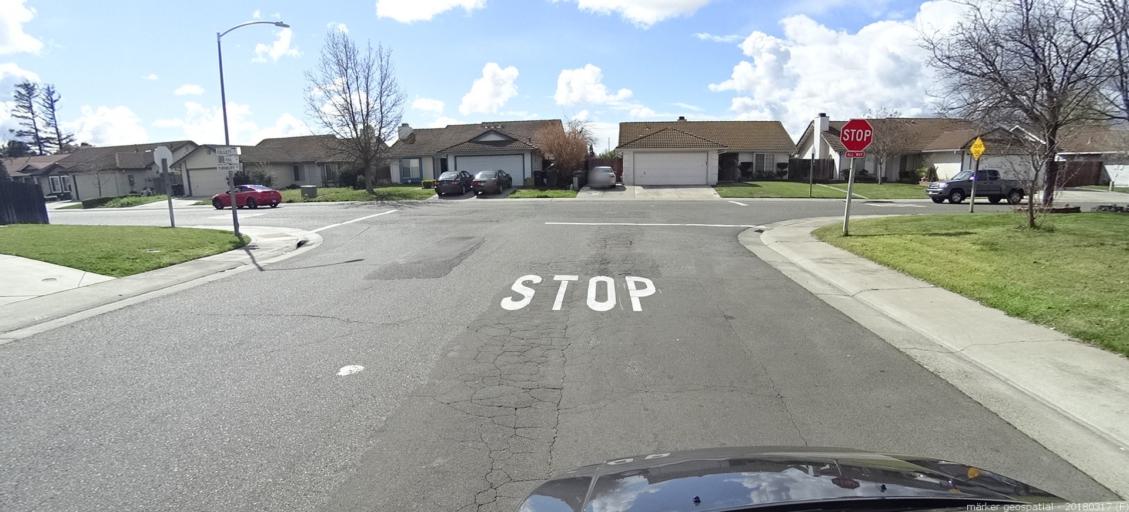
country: US
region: California
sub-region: Sacramento County
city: Florin
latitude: 38.4677
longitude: -121.4048
